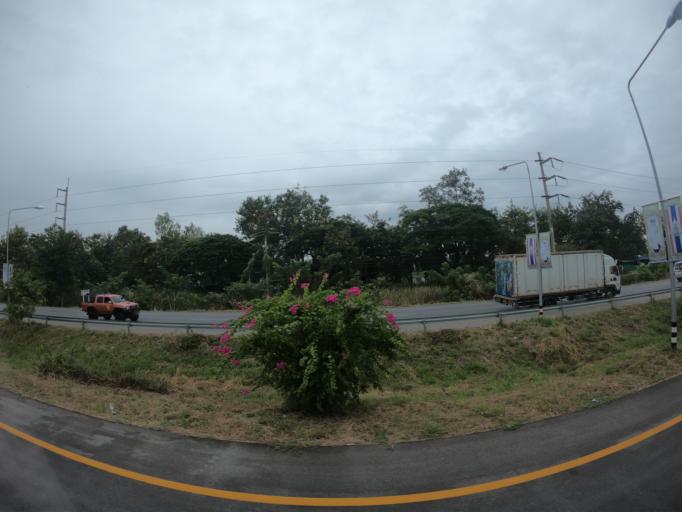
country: TH
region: Maha Sarakham
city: Maha Sarakham
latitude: 16.1426
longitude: 103.2588
